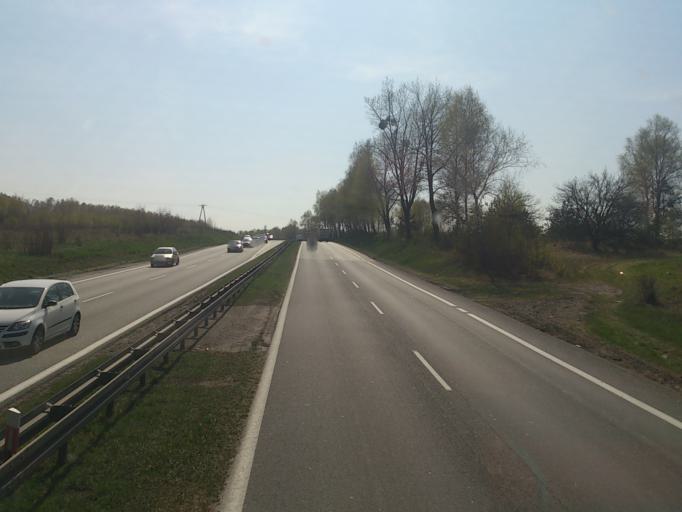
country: PL
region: Silesian Voivodeship
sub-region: Powiat bedzinski
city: Siewierz
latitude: 50.4402
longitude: 19.2185
